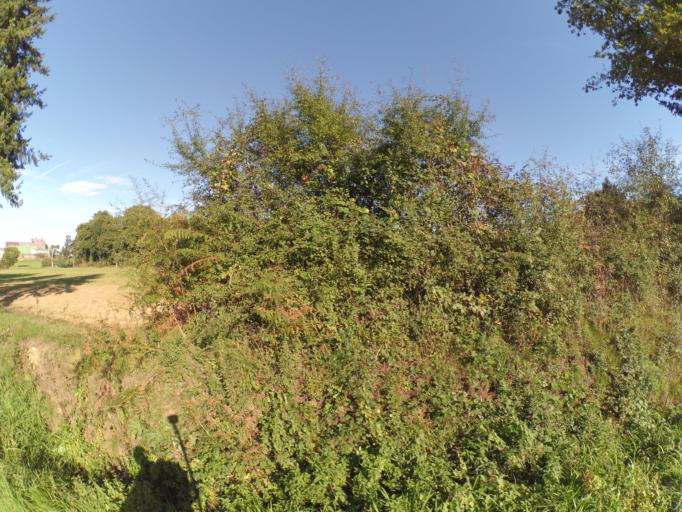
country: FR
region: Brittany
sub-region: Departement du Morbihan
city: Peillac
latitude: 47.7325
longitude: -2.2122
